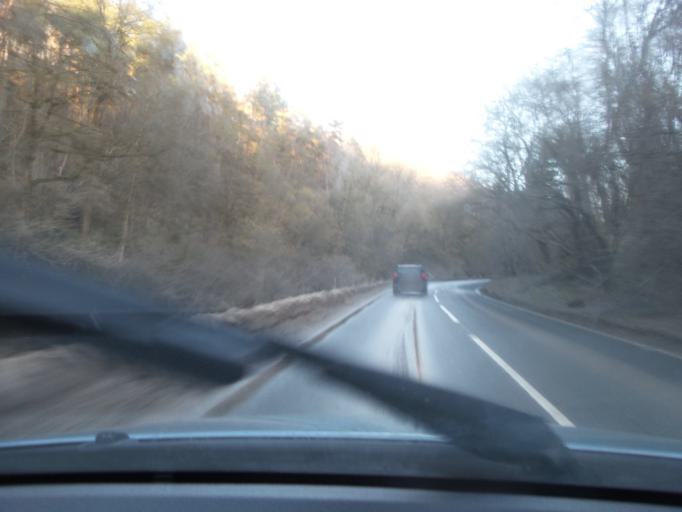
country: GB
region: England
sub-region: Derbyshire
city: Wirksworth
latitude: 53.1069
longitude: -1.6253
